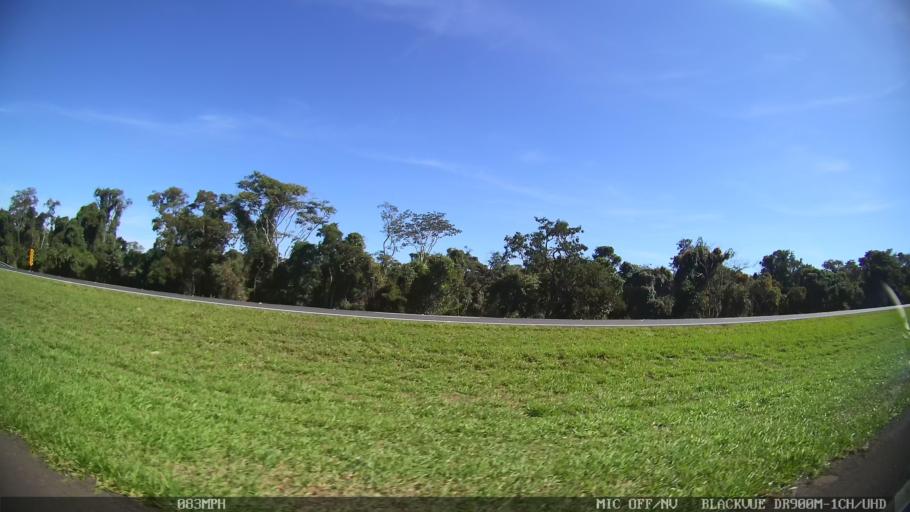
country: BR
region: Sao Paulo
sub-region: Sao Simao
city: Sao Simao
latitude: -21.6252
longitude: -47.6145
